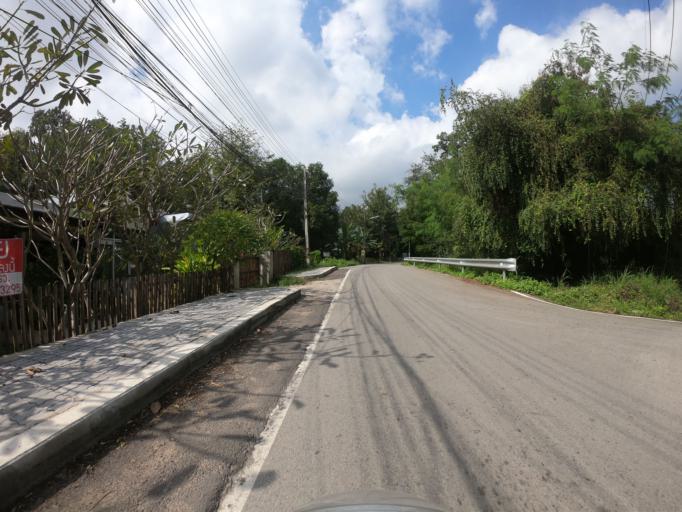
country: TH
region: Chiang Mai
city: Chiang Mai
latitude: 18.8144
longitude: 98.9658
